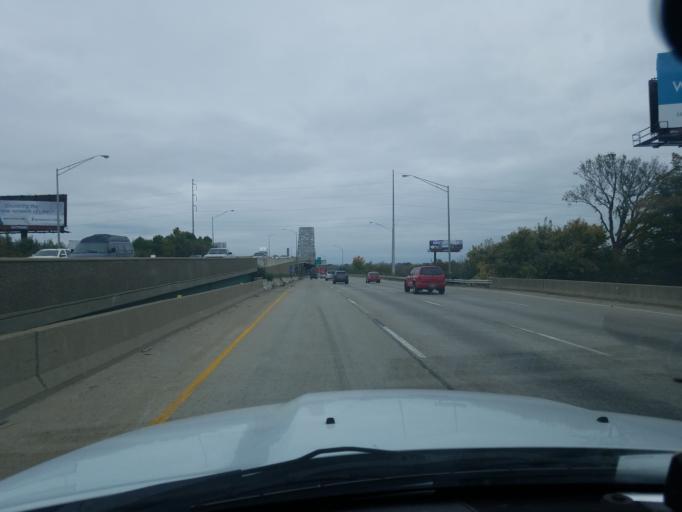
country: US
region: Indiana
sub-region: Floyd County
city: New Albany
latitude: 38.2835
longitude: -85.8273
